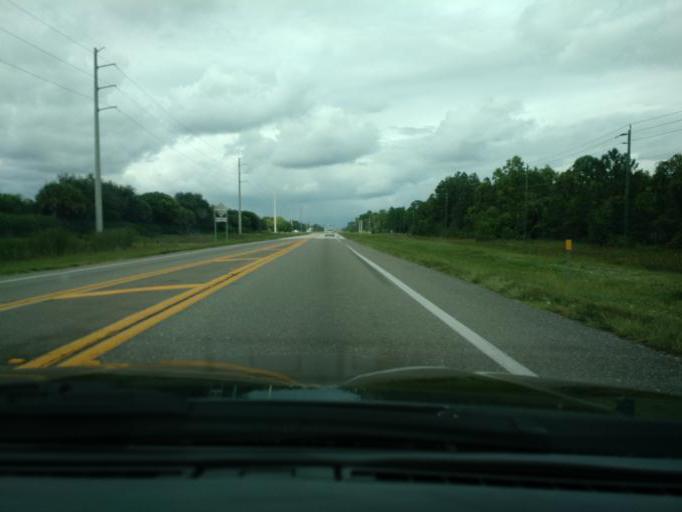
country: US
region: Florida
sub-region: Lee County
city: Gateway
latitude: 26.6049
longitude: -81.7520
